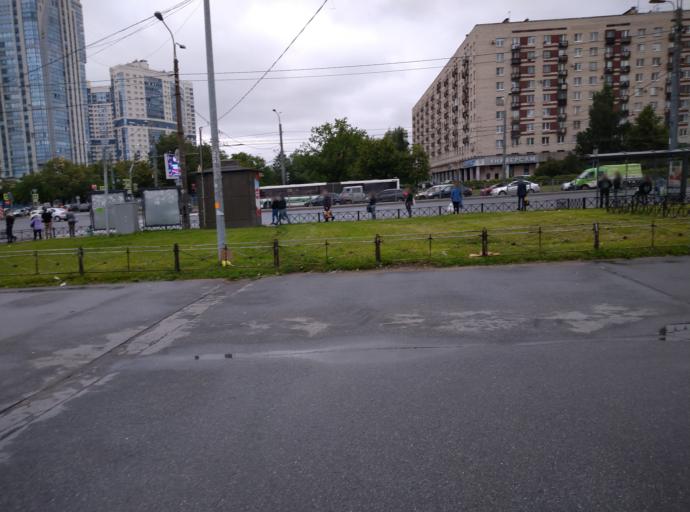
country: RU
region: St.-Petersburg
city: Kupchino
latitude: 59.8524
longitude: 30.3534
